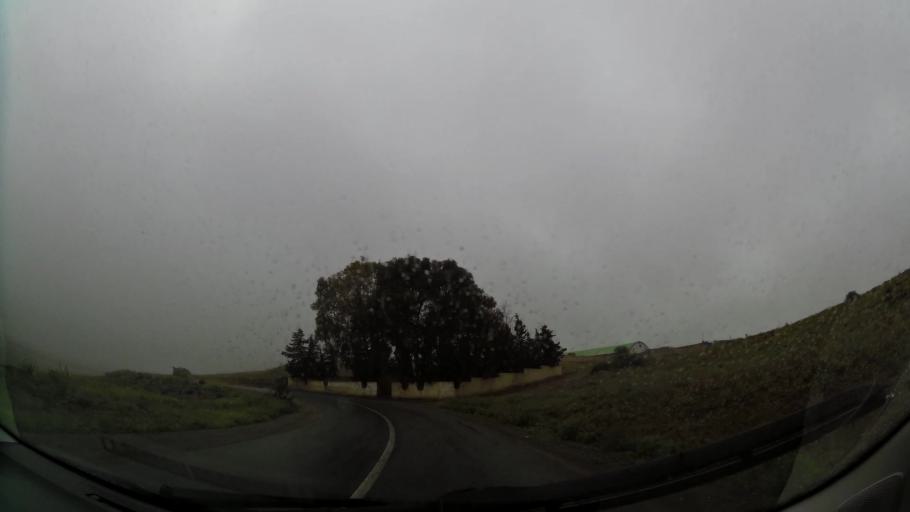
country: MA
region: Oriental
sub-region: Nador
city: Boudinar
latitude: 35.1372
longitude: -3.6001
